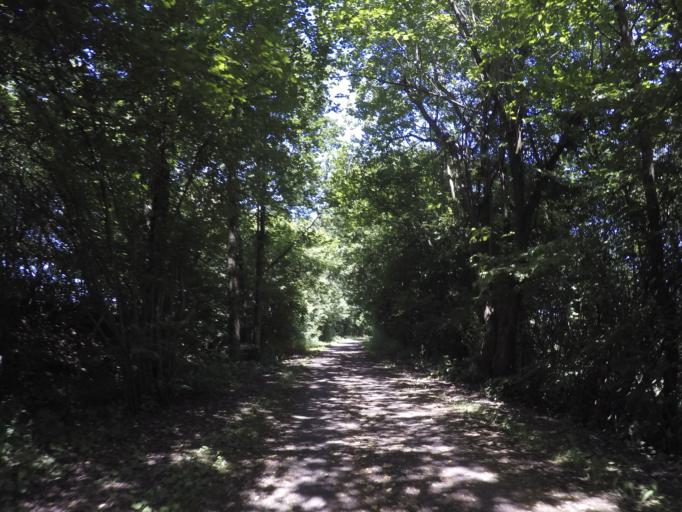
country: BE
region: Wallonia
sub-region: Province de Namur
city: Hamois
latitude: 50.3523
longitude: 5.1753
